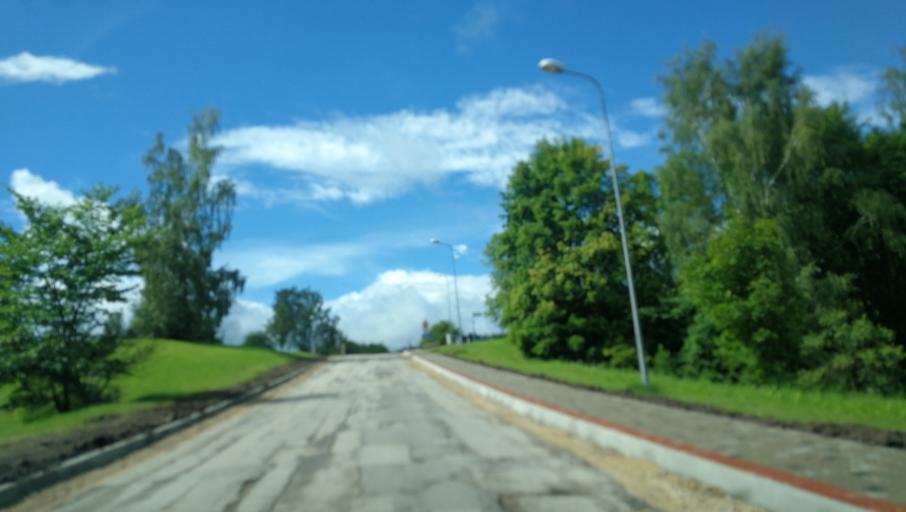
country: LV
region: Cesu Rajons
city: Cesis
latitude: 57.3120
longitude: 25.2578
